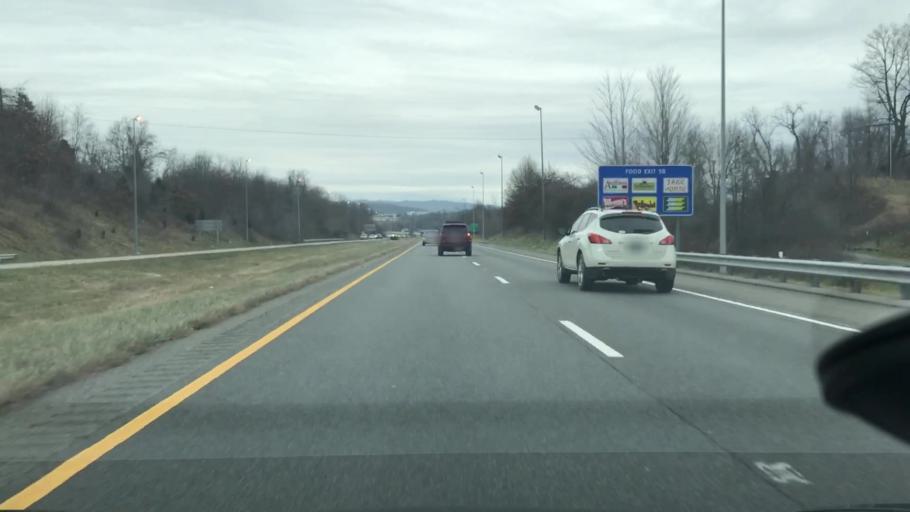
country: US
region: Virginia
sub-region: Montgomery County
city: Merrimac
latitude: 37.1788
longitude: -80.4102
